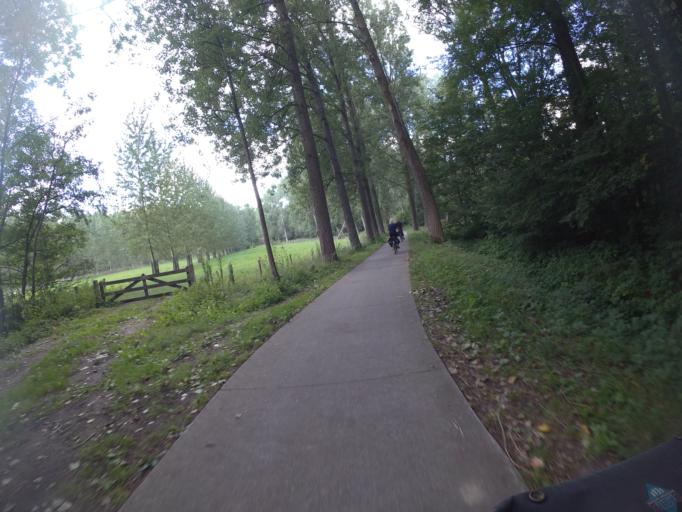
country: NL
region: North Brabant
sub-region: Gemeente Schijndel
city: Schijndel
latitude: 51.6338
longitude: 5.4665
